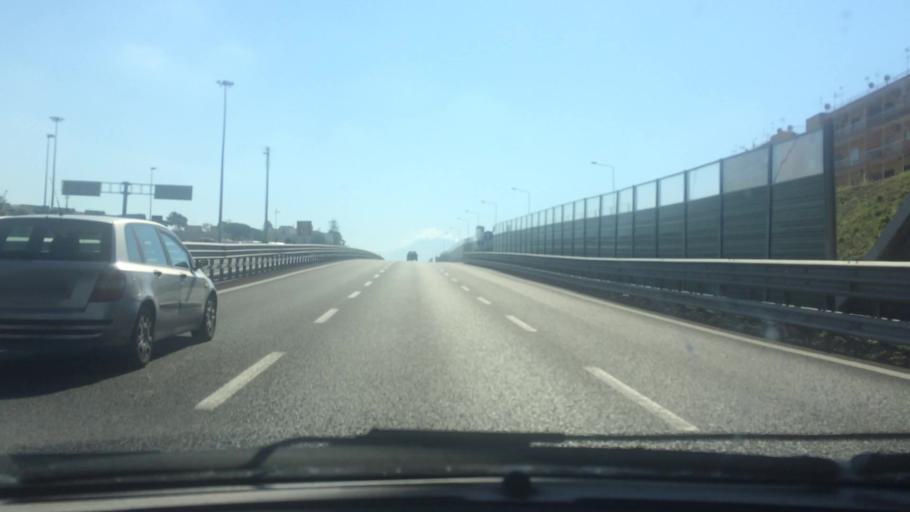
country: IT
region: Campania
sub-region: Provincia di Napoli
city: Ercolano
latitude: 40.8167
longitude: 14.3548
